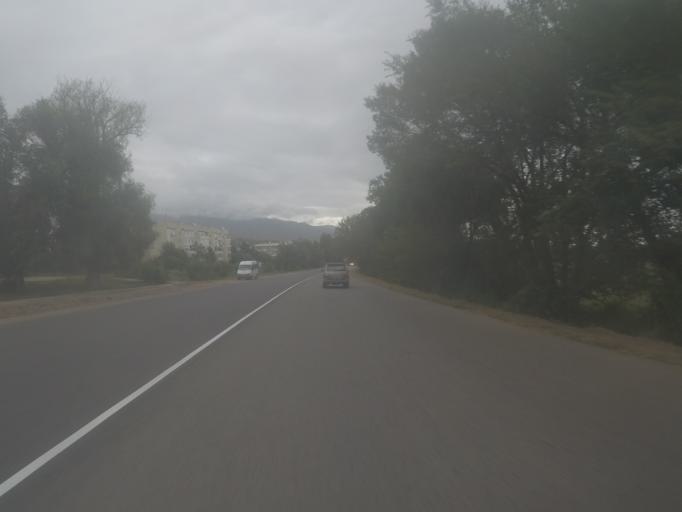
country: KG
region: Ysyk-Koel
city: Cholpon-Ata
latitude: 42.6733
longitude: 77.2968
